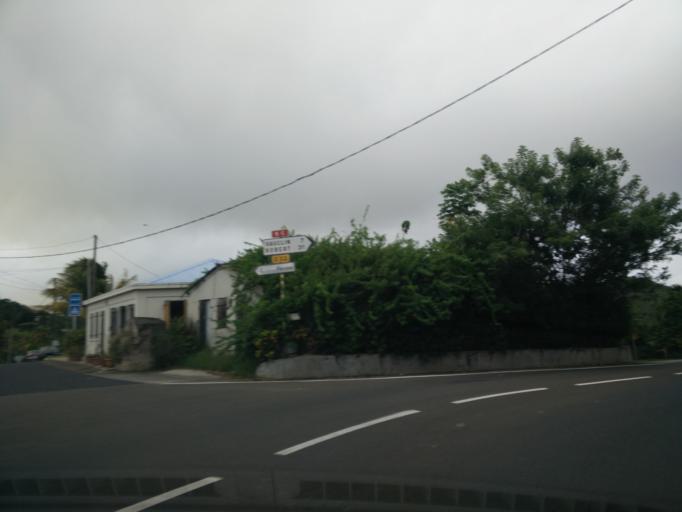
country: MQ
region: Martinique
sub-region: Martinique
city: Le Marin
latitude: 14.4938
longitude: -60.8600
